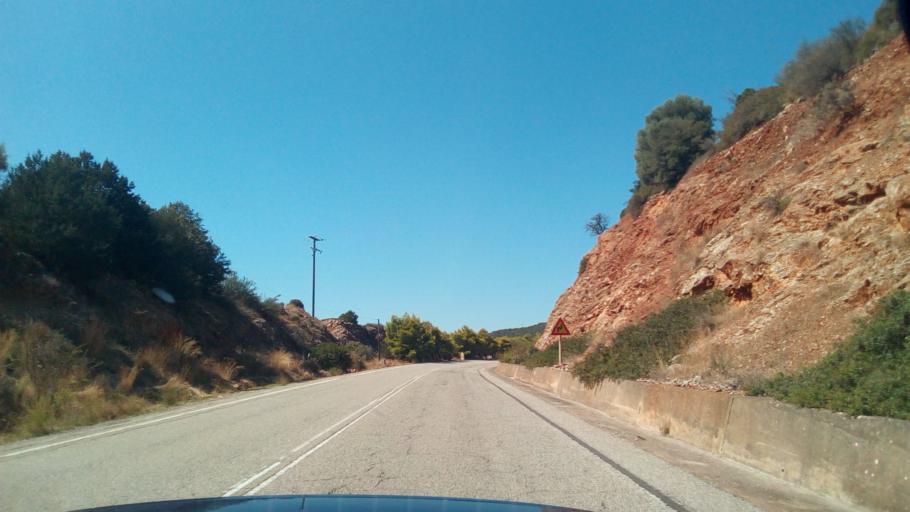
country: GR
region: West Greece
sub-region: Nomos Achaias
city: Selianitika
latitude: 38.3685
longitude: 22.1131
